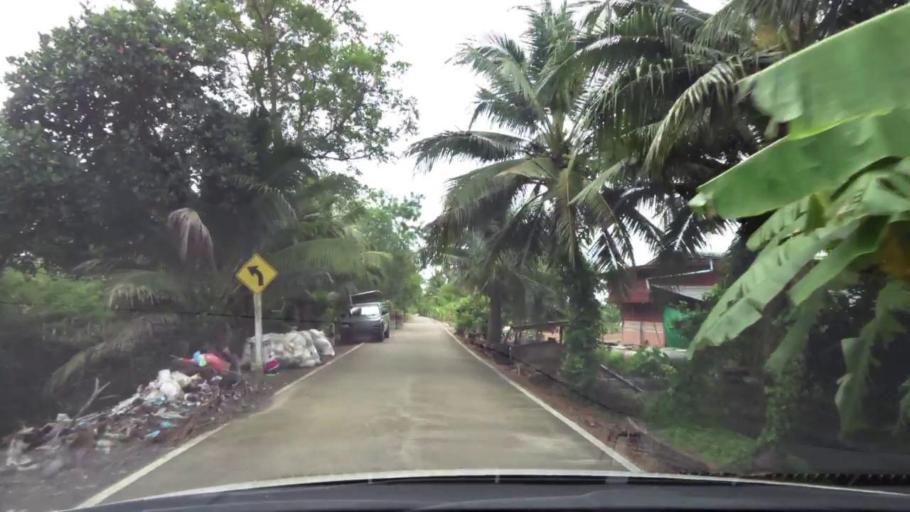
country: TH
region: Ratchaburi
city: Damnoen Saduak
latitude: 13.5531
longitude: 99.9843
